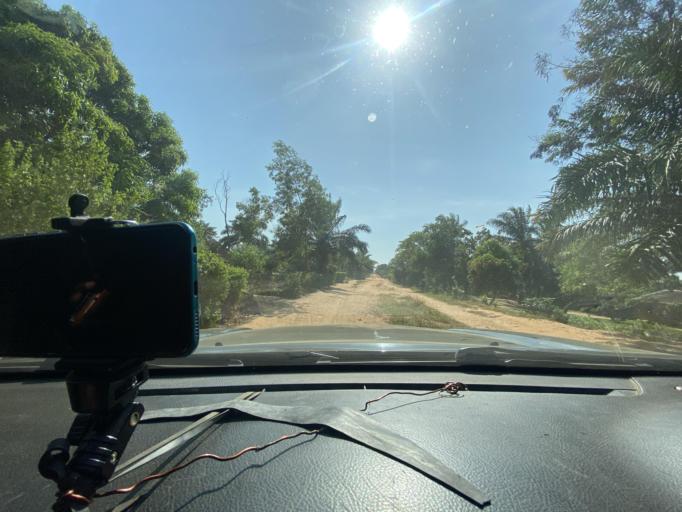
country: CD
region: Kasai-Oriental
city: Kabinda
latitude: -6.1323
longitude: 24.5131
